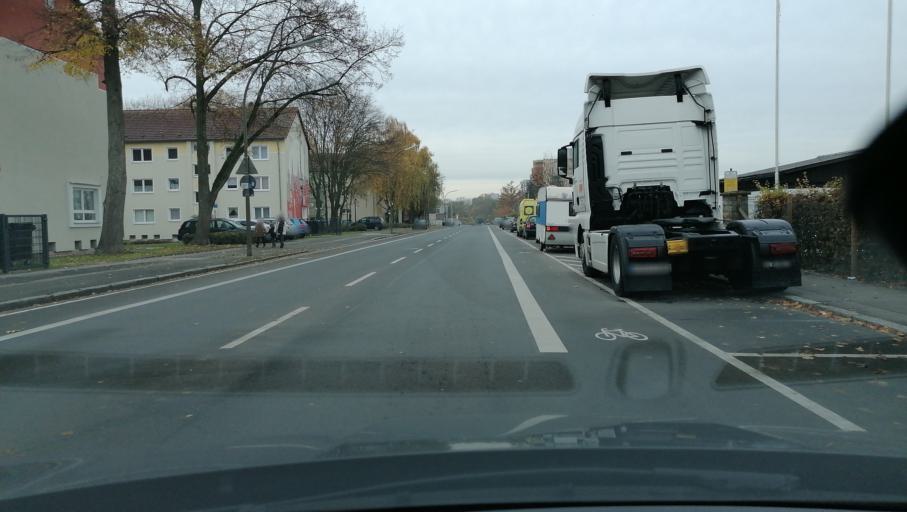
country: DE
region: North Rhine-Westphalia
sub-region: Regierungsbezirk Arnsberg
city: Dortmund
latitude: 51.4979
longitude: 7.5018
